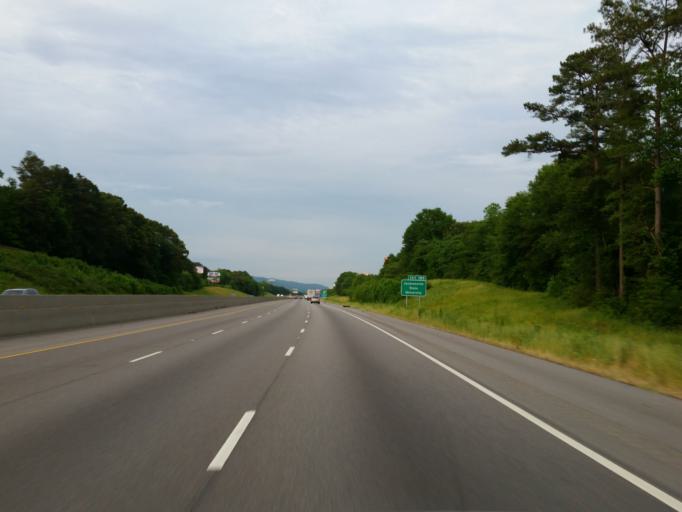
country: US
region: Alabama
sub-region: Calhoun County
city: Oxford
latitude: 33.5957
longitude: -85.8543
